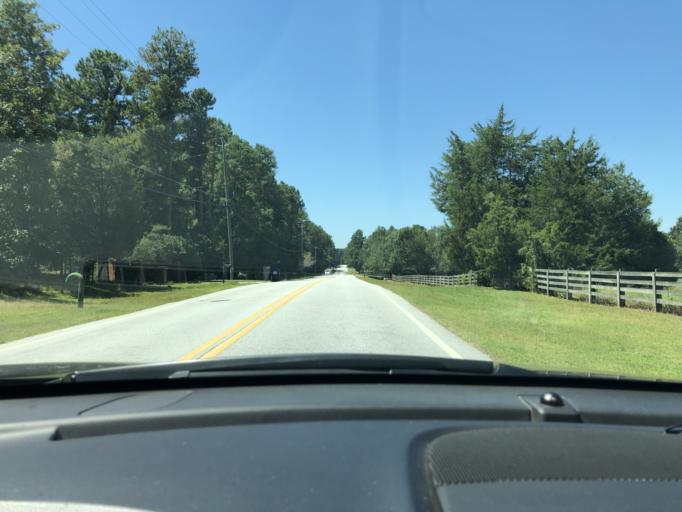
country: US
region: Georgia
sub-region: Gwinnett County
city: Grayson
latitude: 33.9042
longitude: -83.8909
